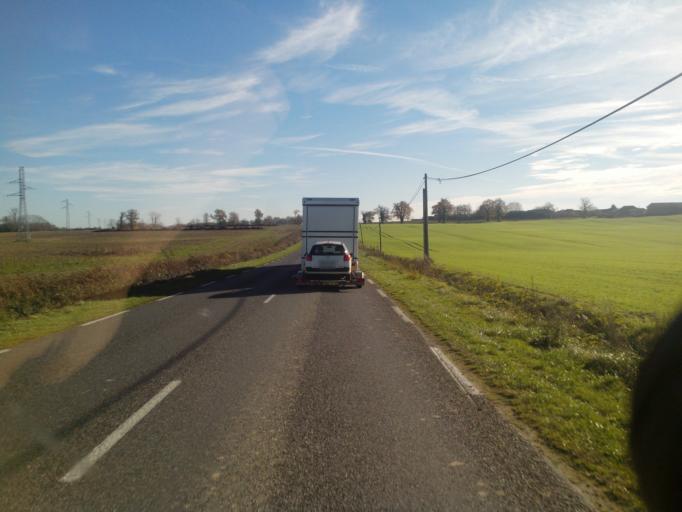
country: FR
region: Limousin
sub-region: Departement de la Haute-Vienne
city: Bellac
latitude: 46.0810
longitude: 1.0906
